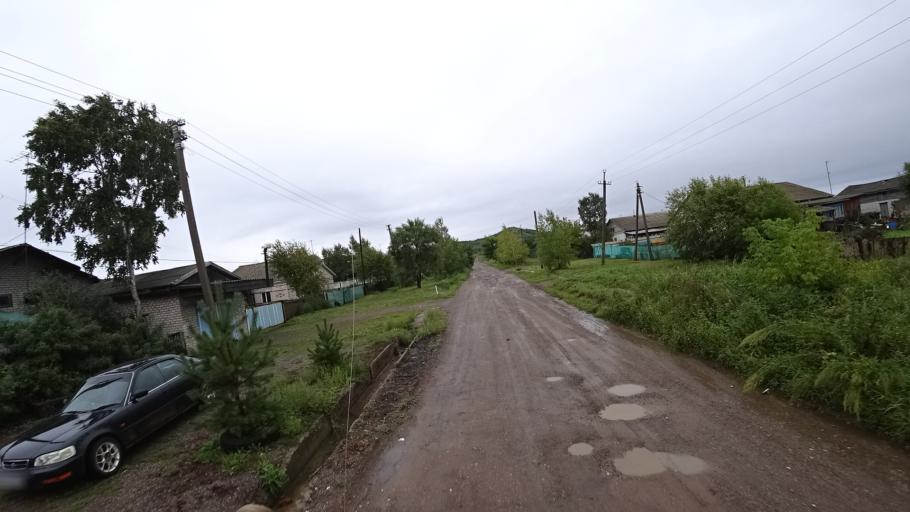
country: RU
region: Primorskiy
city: Monastyrishche
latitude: 44.2316
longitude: 132.4596
